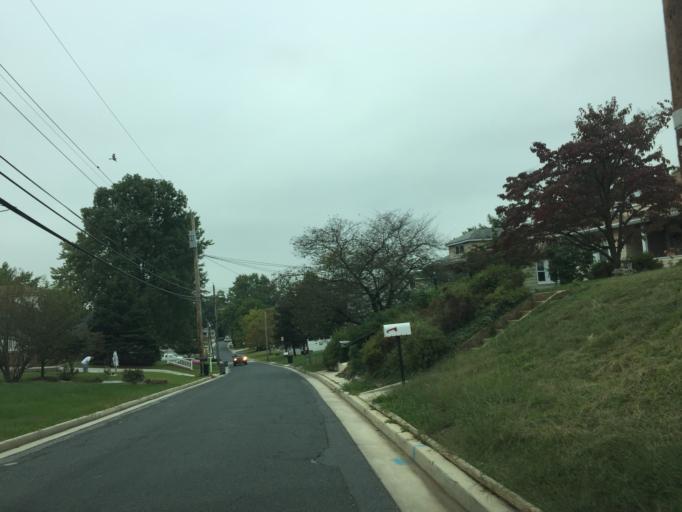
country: US
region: Maryland
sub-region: Baltimore County
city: Rosedale
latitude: 39.3218
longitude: -76.5106
